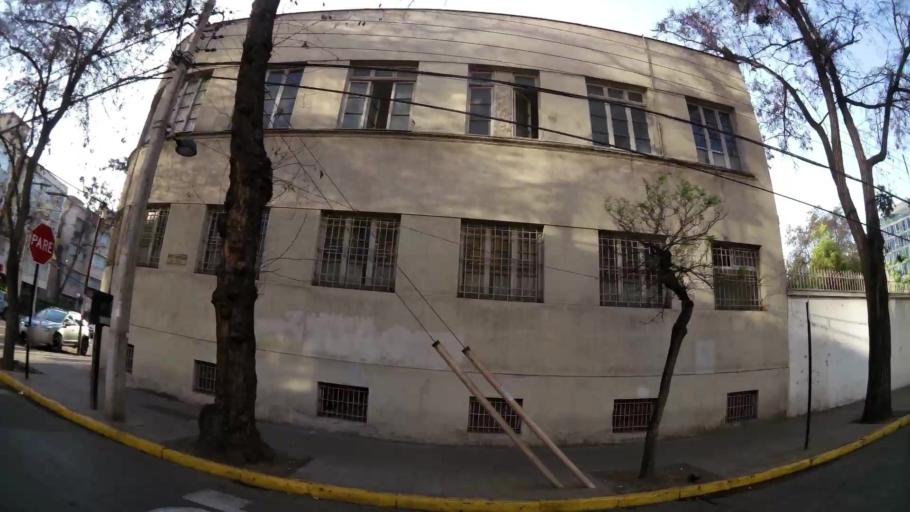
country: CL
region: Santiago Metropolitan
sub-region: Provincia de Santiago
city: Santiago
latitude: -33.4277
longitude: -70.6212
